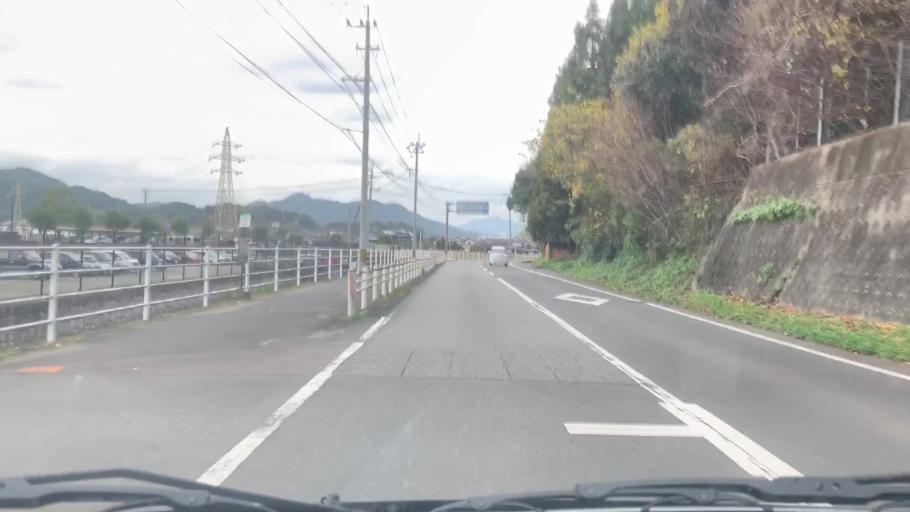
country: JP
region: Saga Prefecture
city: Kashima
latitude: 33.1186
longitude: 130.0637
